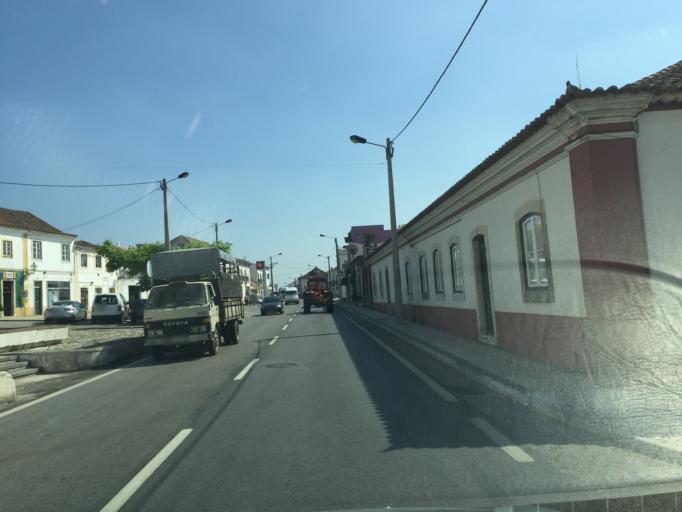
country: PT
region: Santarem
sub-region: Golega
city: Golega
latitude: 39.3557
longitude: -8.4835
